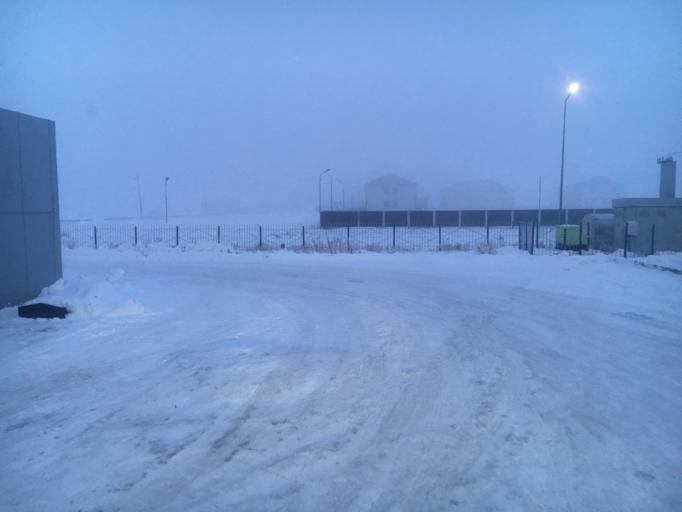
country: KZ
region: Batys Qazaqstan
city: Dzhambeyty
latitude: 50.2588
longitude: 52.6219
